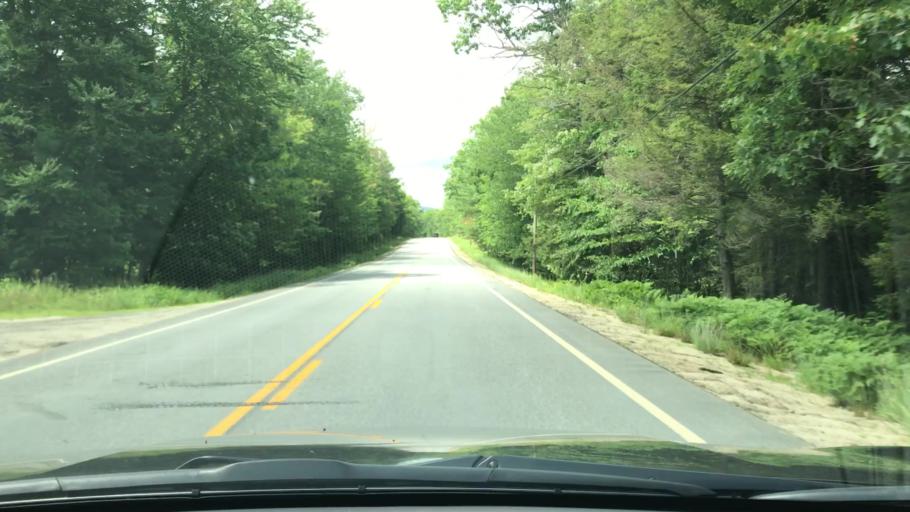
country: US
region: Maine
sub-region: Oxford County
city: Hartford
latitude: 44.3711
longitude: -70.4000
